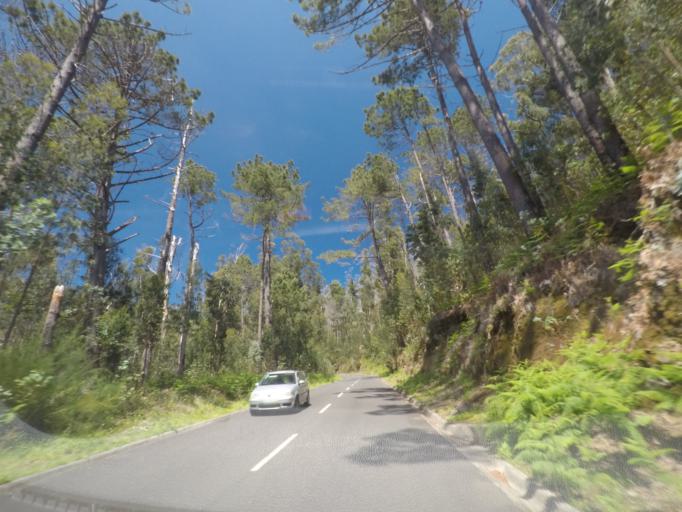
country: PT
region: Madeira
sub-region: Calheta
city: Arco da Calheta
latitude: 32.7340
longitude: -17.1303
